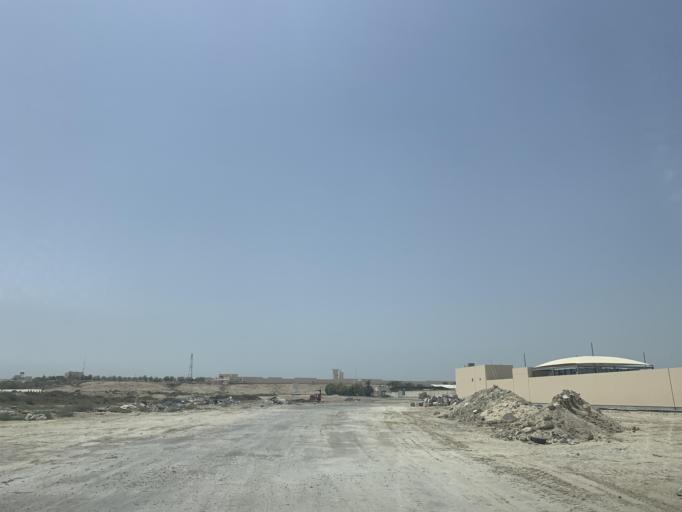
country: BH
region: Central Governorate
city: Madinat Hamad
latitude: 26.1560
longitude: 50.4915
